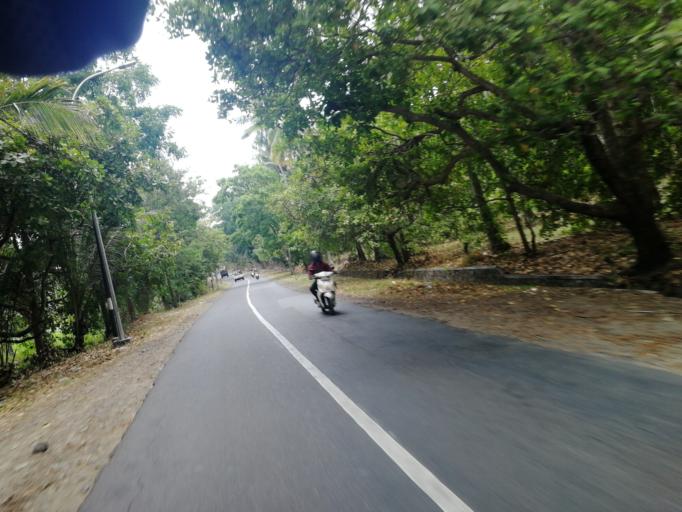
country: ID
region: West Nusa Tenggara
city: Karangsubagan
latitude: -8.4211
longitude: 116.0942
